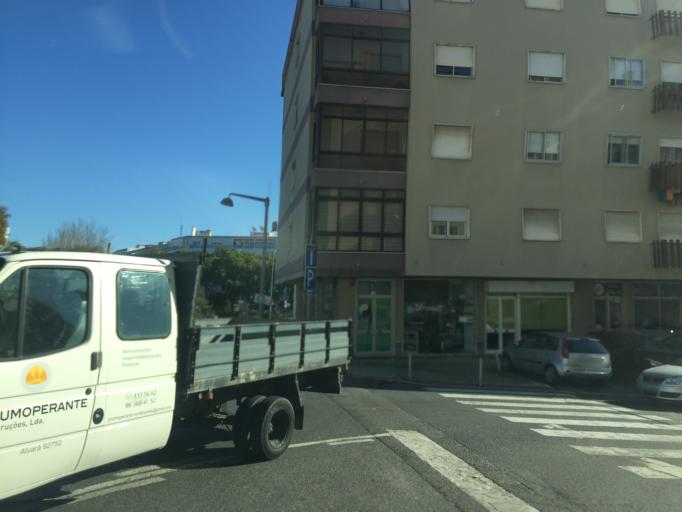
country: PT
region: Lisbon
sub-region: Sintra
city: Queluz
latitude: 38.7573
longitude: -9.2496
